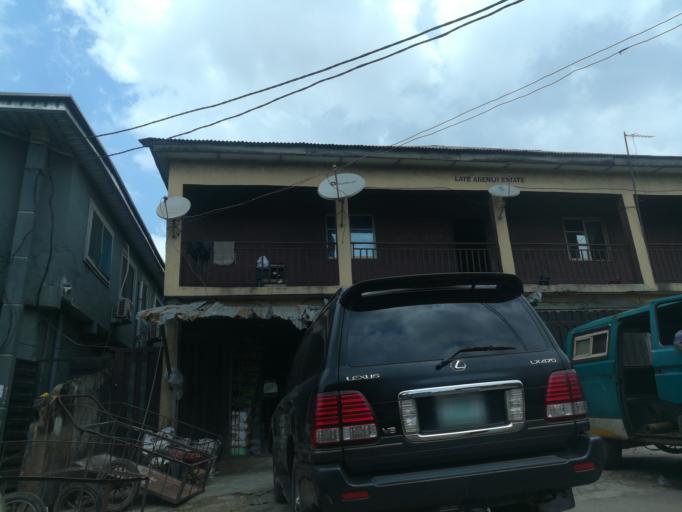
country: NG
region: Lagos
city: Mushin
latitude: 6.5278
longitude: 3.3566
